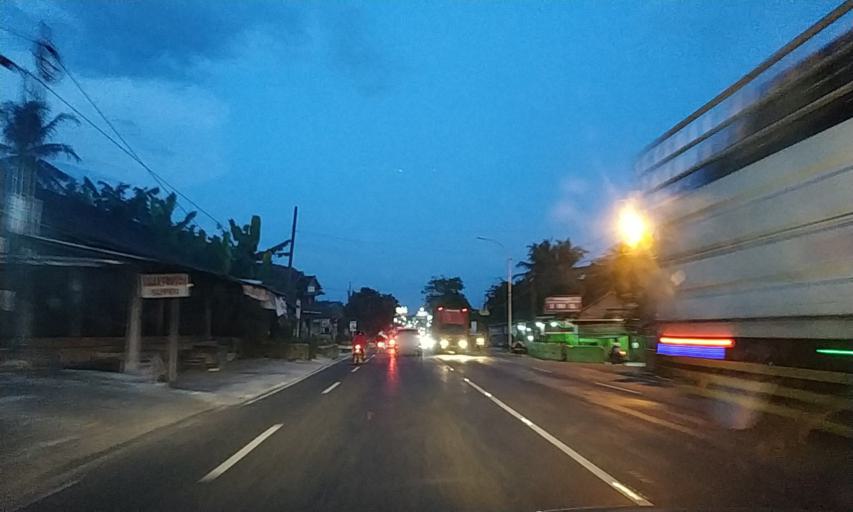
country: ID
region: Daerah Istimewa Yogyakarta
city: Godean
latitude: -7.8131
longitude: 110.2642
